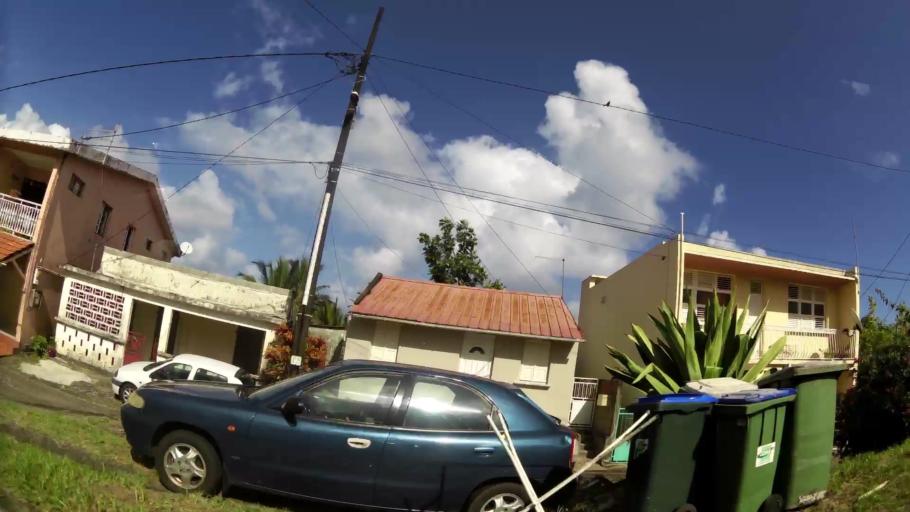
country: MQ
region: Martinique
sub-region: Martinique
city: Le Lorrain
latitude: 14.8324
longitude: -61.0492
